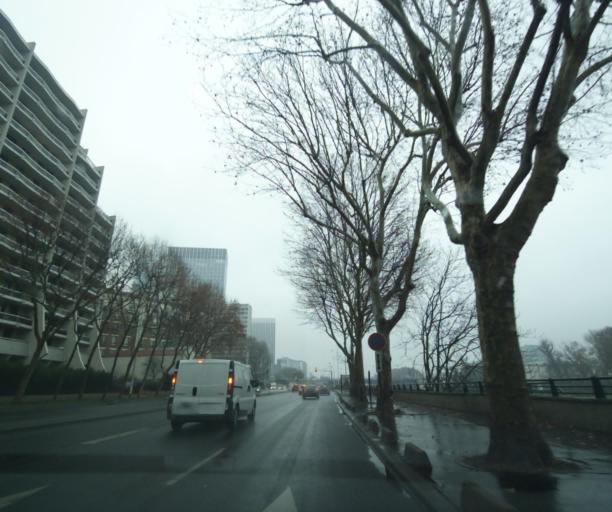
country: FR
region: Ile-de-France
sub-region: Departement des Hauts-de-Seine
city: Puteaux
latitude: 48.8845
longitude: 2.2502
